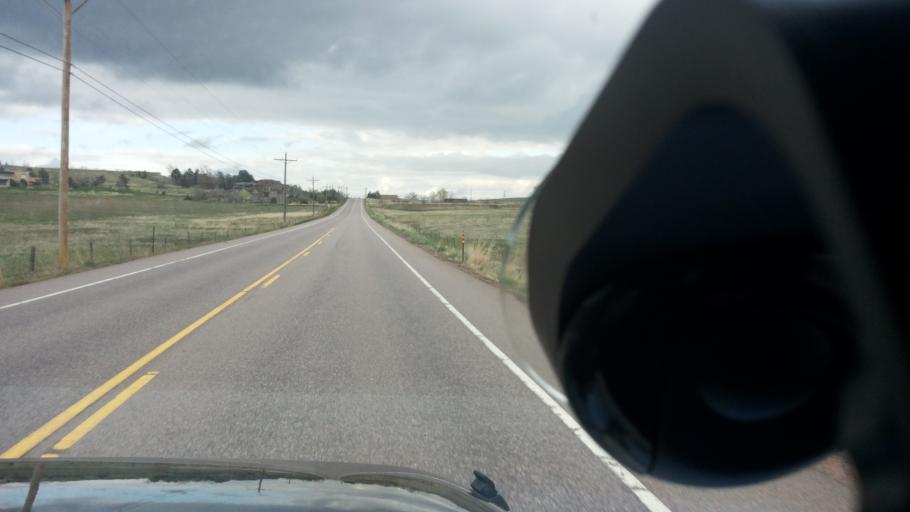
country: US
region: Colorado
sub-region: Boulder County
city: Superior
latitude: 39.9615
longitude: -105.1986
